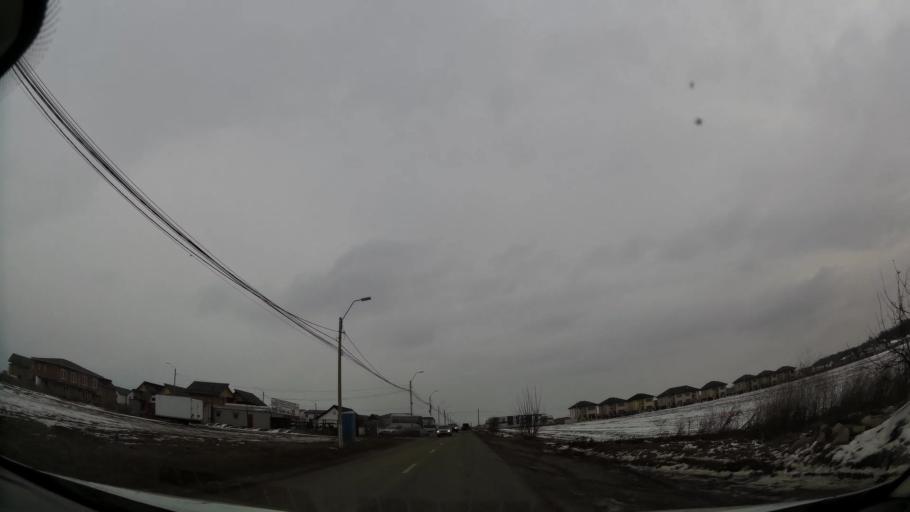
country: RO
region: Ilfov
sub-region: Comuna Tunari
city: Tunari
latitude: 44.5523
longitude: 26.1097
